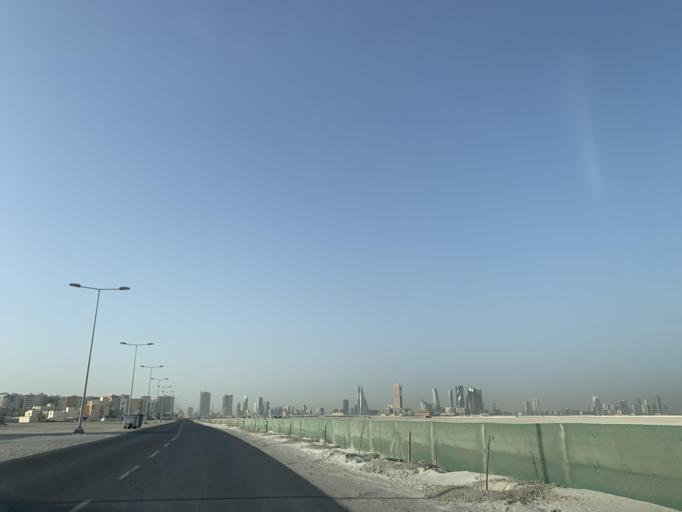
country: BH
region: Muharraq
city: Al Muharraq
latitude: 26.2761
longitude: 50.5945
